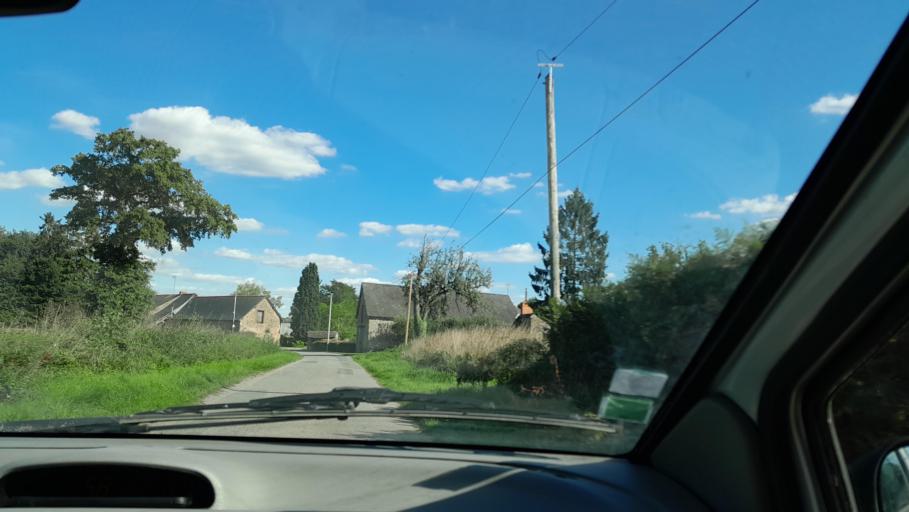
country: FR
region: Pays de la Loire
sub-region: Departement de la Mayenne
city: Ballots
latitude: 47.9543
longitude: -1.0732
